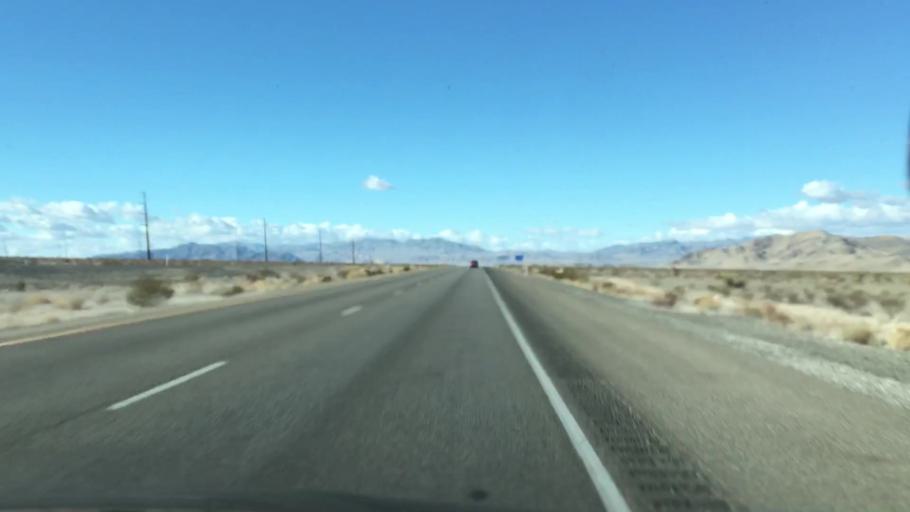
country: US
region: Nevada
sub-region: Clark County
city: Summerlin South
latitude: 36.5526
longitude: -115.5978
